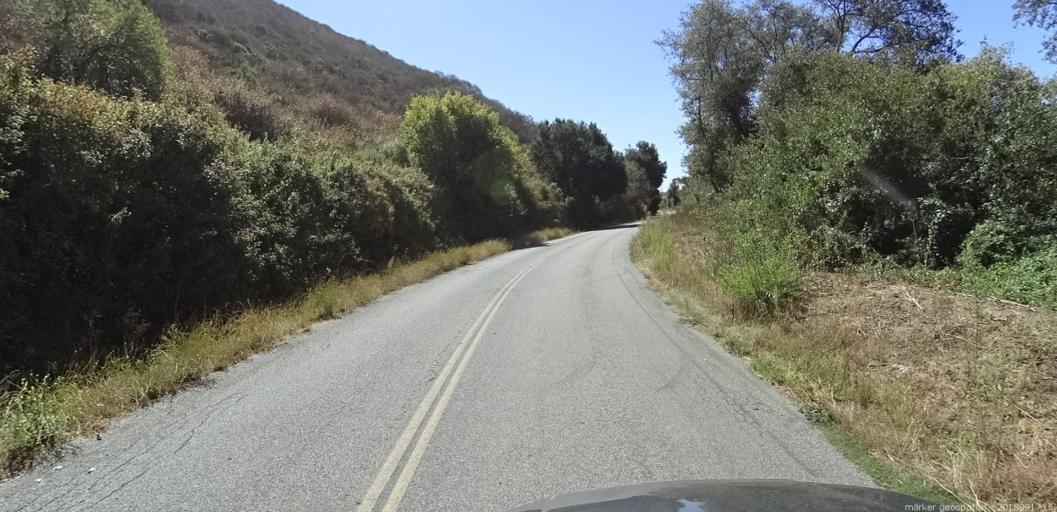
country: US
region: California
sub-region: Monterey County
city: Prunedale
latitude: 36.7677
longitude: -121.6017
